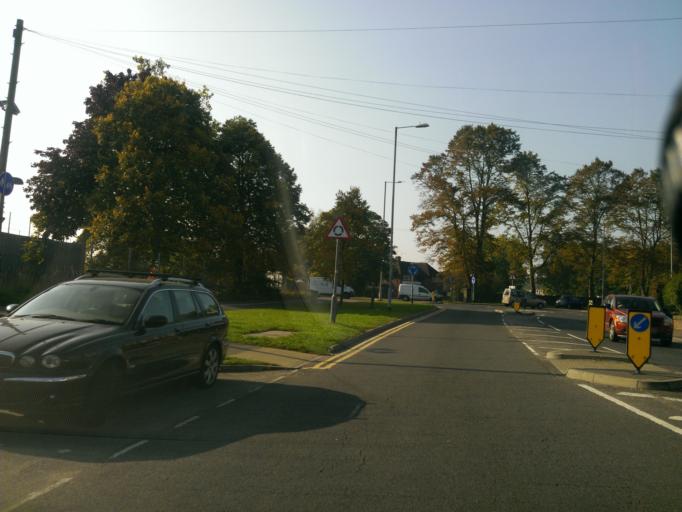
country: GB
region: England
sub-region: Essex
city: Colchester
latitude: 51.8805
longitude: 0.8878
